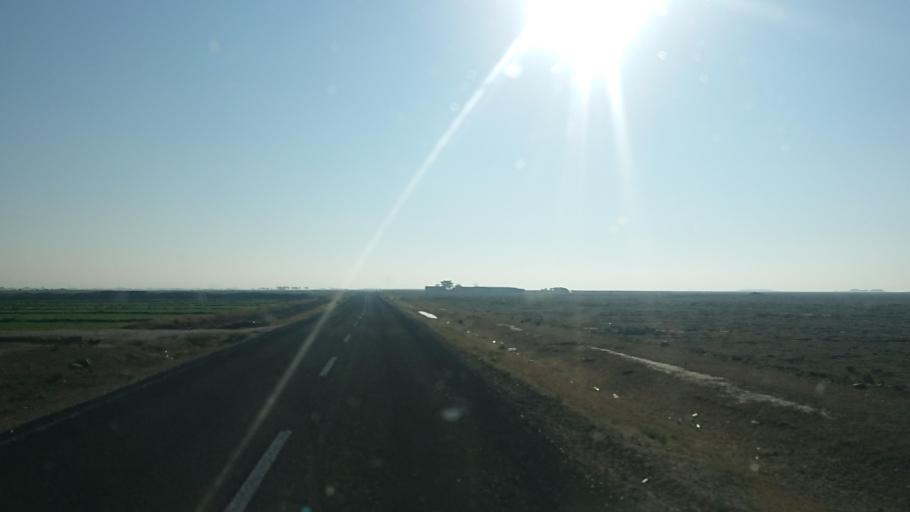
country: TR
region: Aksaray
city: Yesilova
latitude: 38.3876
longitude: 33.7991
